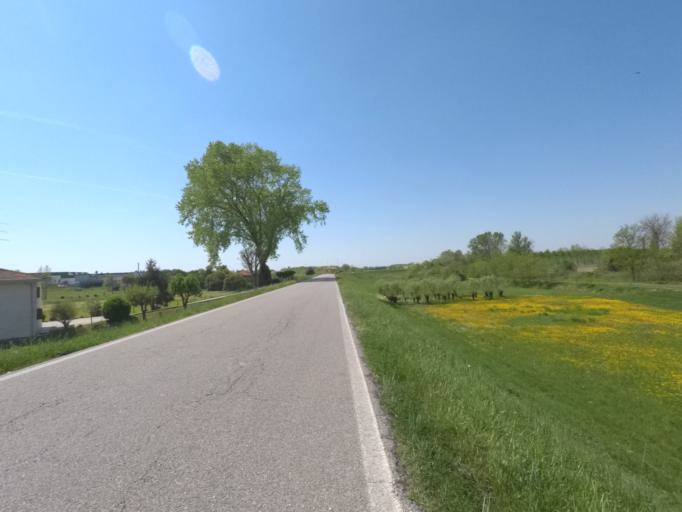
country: IT
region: Veneto
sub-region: Provincia di Treviso
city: Mansue
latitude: 45.8260
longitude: 12.5641
